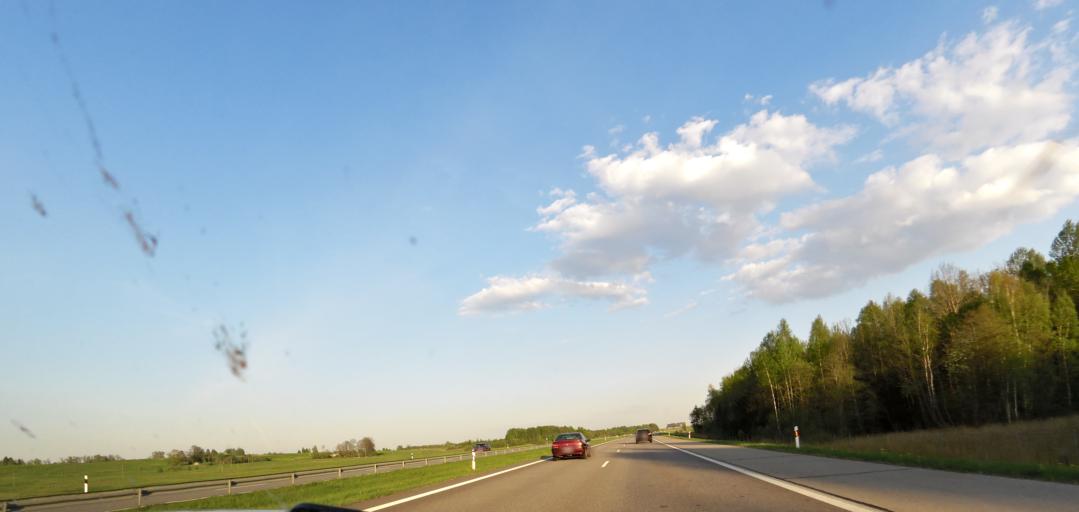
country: LT
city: Sirvintos
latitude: 54.9045
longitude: 25.0310
